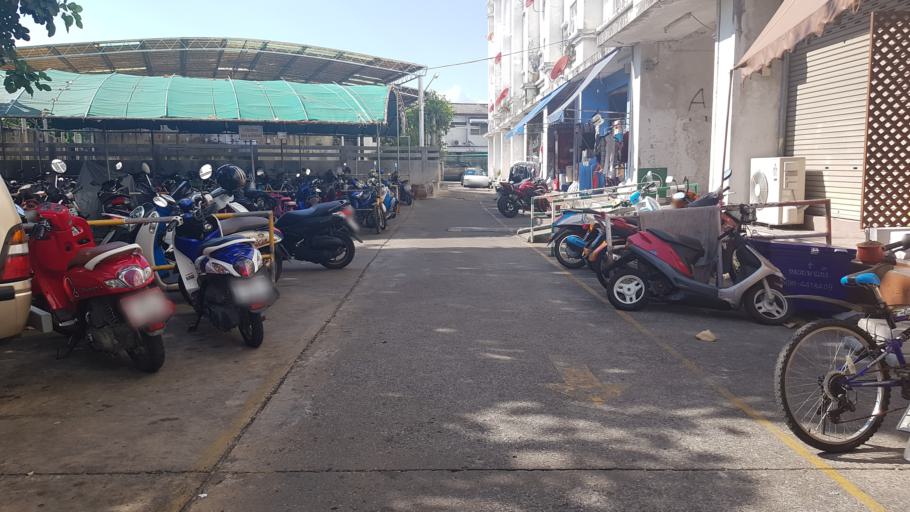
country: TH
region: Bangkok
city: Wang Thonglang
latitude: 13.7822
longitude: 100.6255
